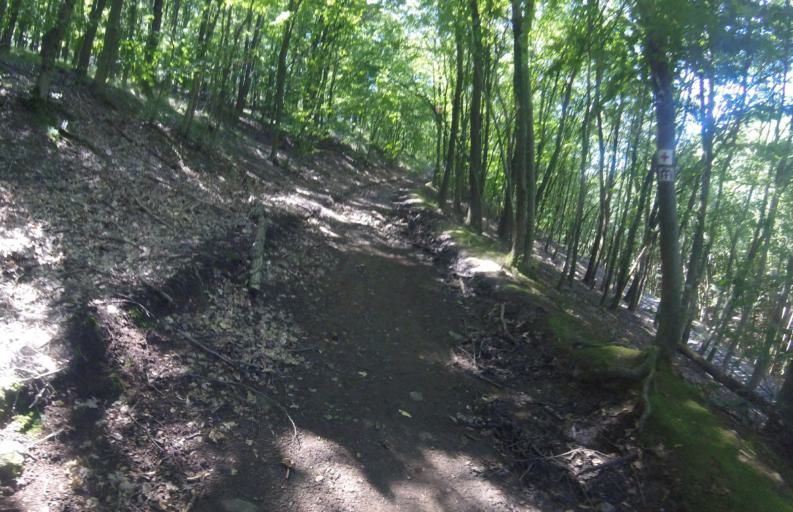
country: HU
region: Pest
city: Szob
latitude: 47.8878
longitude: 18.8701
